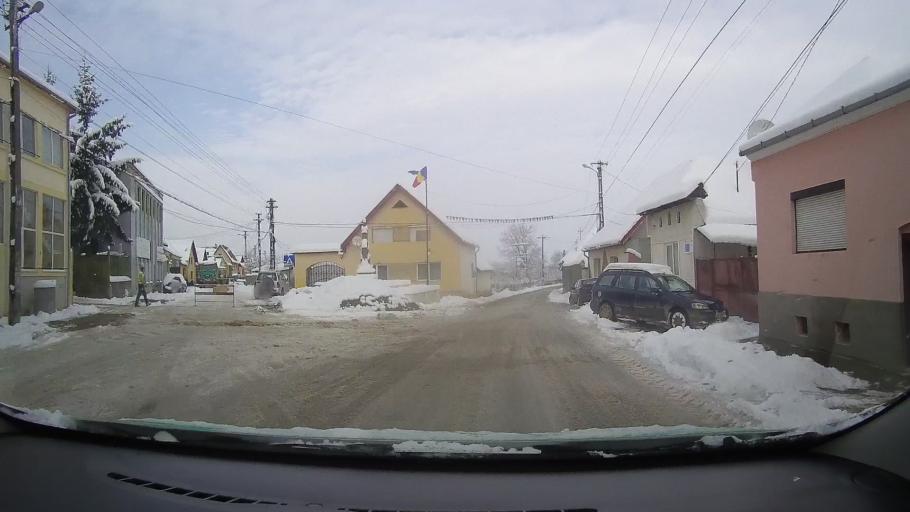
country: RO
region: Alba
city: Pianu de Sus
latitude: 45.9031
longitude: 23.4804
